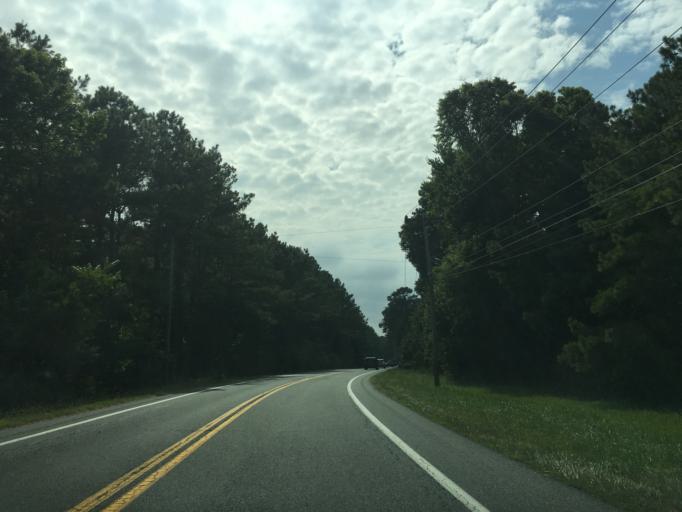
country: US
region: Delaware
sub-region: Sussex County
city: Bethany Beach
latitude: 38.5555
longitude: -75.0678
